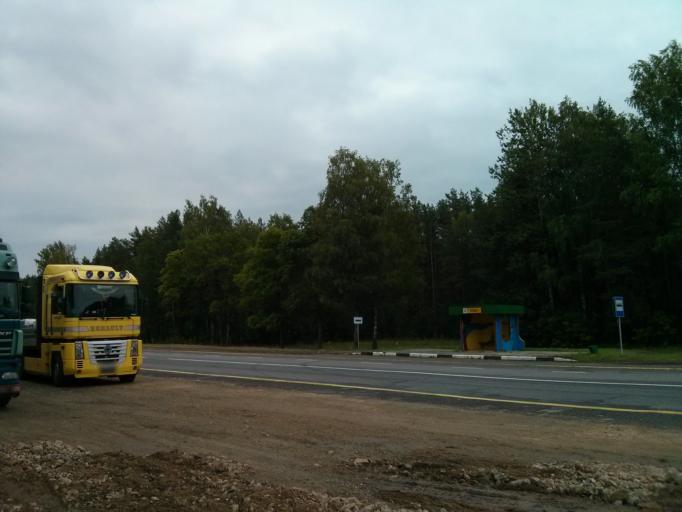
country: BY
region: Vitebsk
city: Lyepyel'
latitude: 54.8204
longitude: 28.6608
